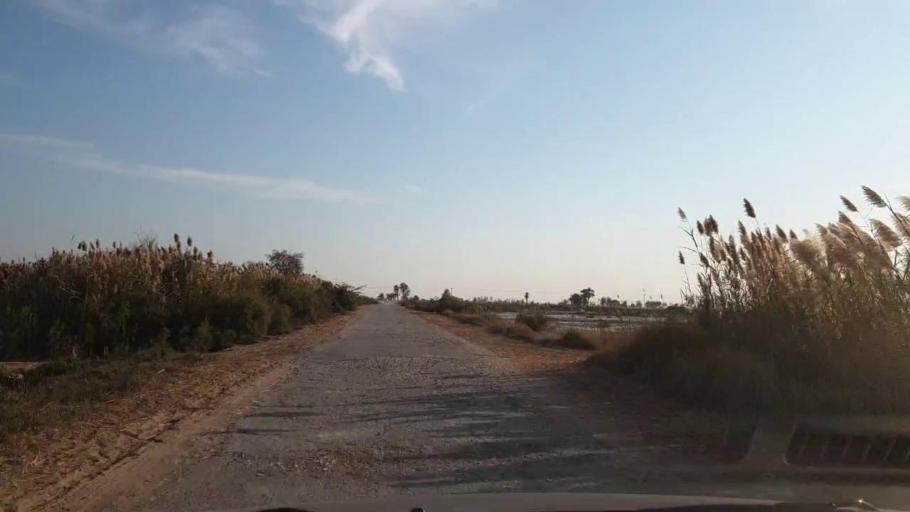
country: PK
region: Sindh
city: Khadro
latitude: 26.1807
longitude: 68.7501
